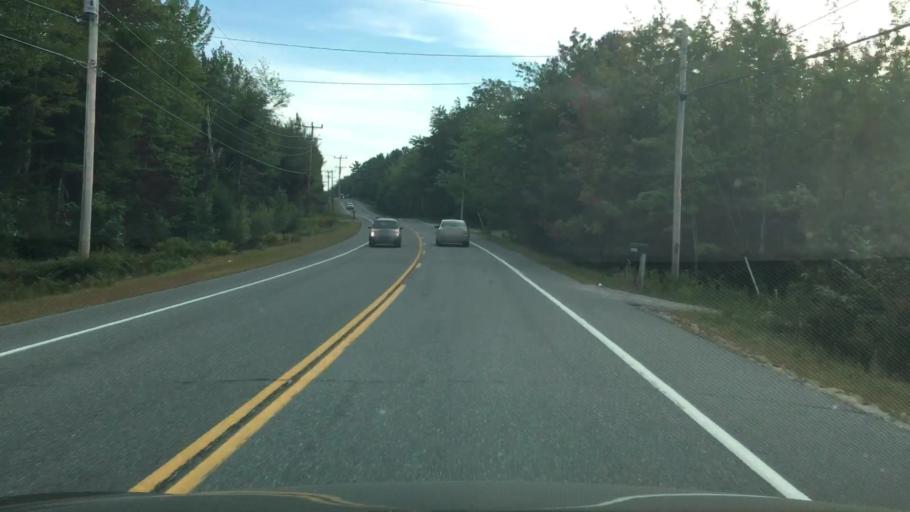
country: US
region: Maine
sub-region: Hancock County
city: Surry
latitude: 44.4546
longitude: -68.5526
